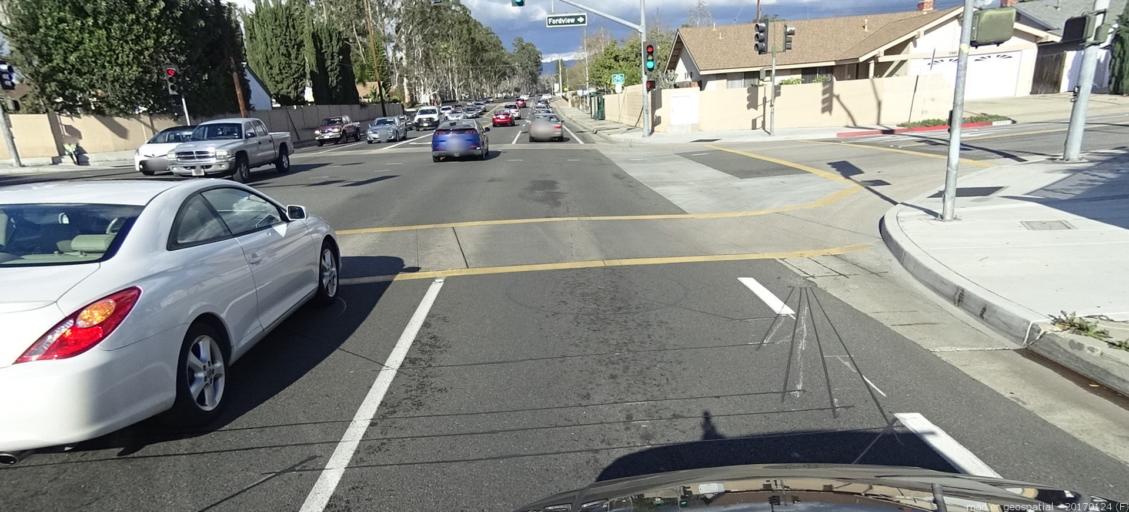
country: US
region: California
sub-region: Orange County
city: Laguna Hills
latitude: 33.6123
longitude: -117.6963
